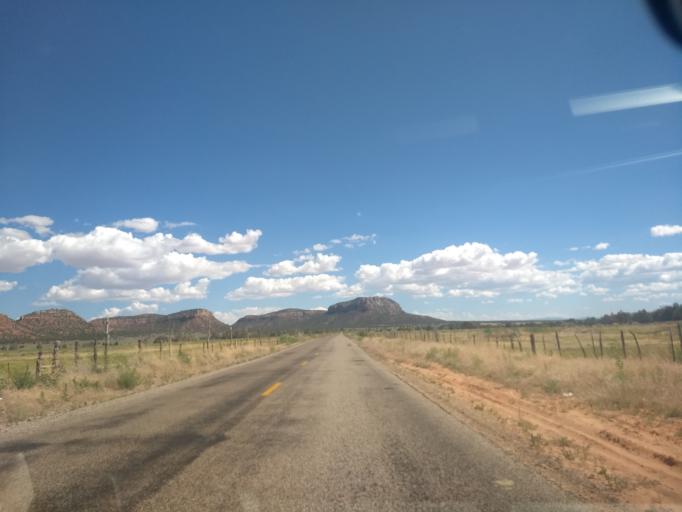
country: US
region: Utah
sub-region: Washington County
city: Hildale
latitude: 36.9578
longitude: -112.8746
